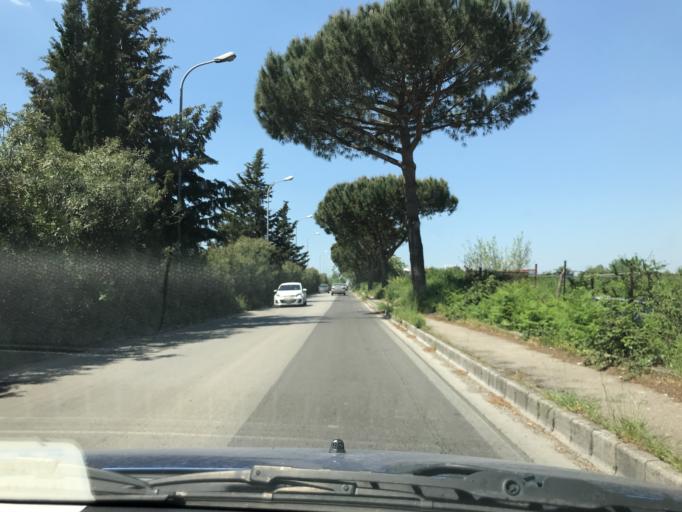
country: IT
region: Campania
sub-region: Provincia di Napoli
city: Calvizzano
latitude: 40.9106
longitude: 14.1918
